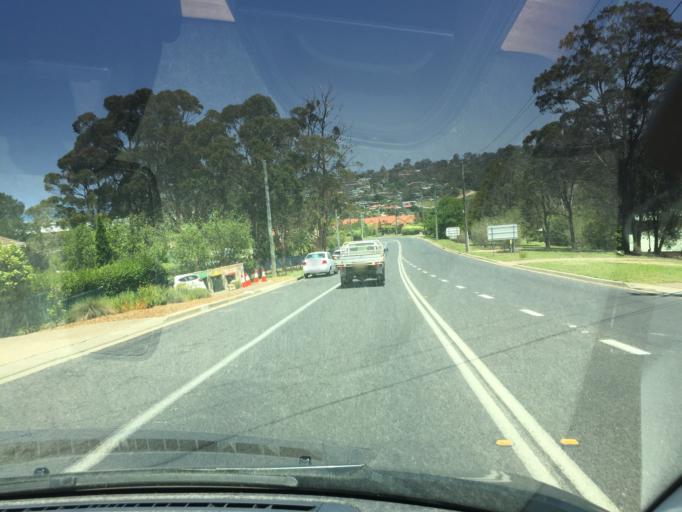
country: AU
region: New South Wales
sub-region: Bega Valley
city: Merimbula
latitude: -36.8797
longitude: 149.9051
